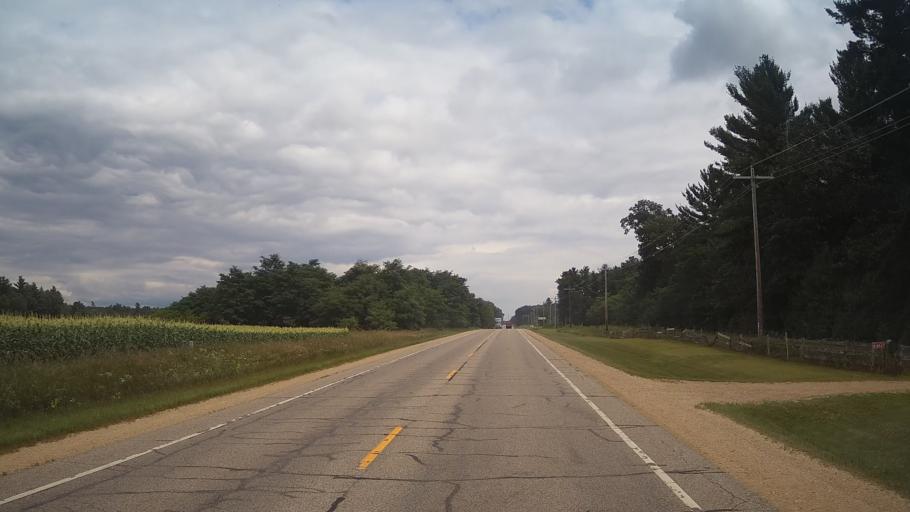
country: US
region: Wisconsin
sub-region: Waushara County
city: Wautoma
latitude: 44.0684
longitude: -89.3304
